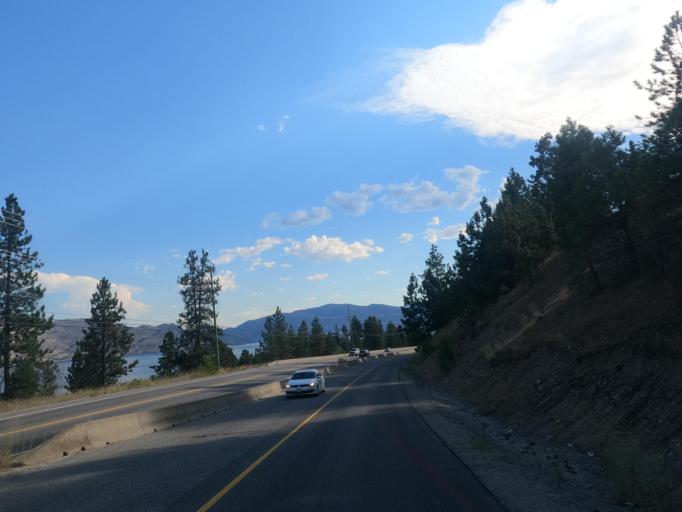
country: CA
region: British Columbia
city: Peachland
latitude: 49.7873
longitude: -119.7096
